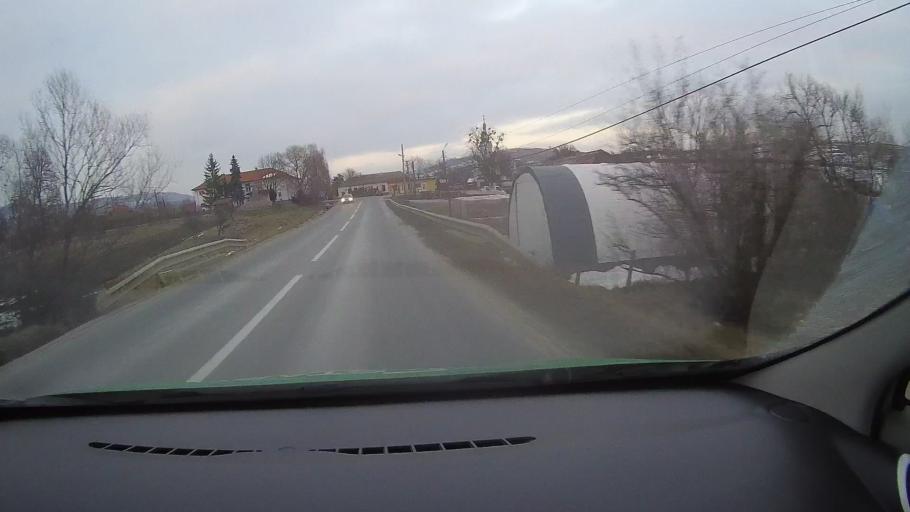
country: RO
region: Harghita
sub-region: Comuna Lupeni
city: Lupeni
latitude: 46.3595
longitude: 25.2369
